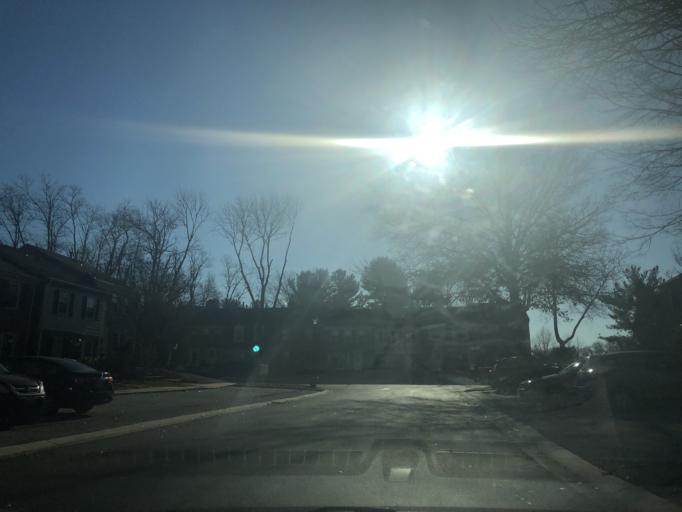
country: US
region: Maryland
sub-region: Howard County
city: Columbia
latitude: 39.2107
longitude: -76.8393
